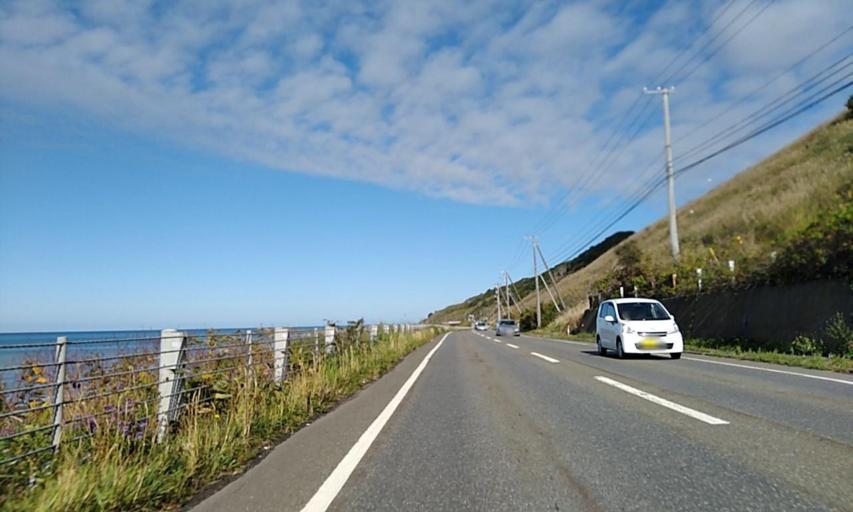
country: JP
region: Hokkaido
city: Shizunai-furukawacho
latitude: 42.3196
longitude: 142.3851
